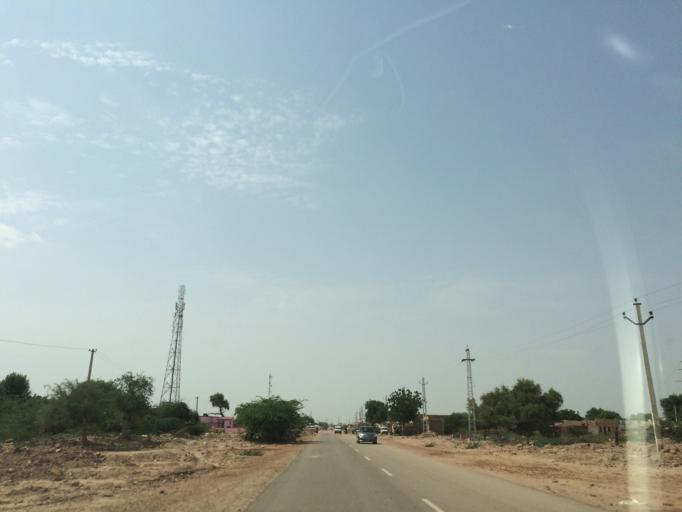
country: IN
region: Rajasthan
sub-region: Jaisalmer
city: Jaisalmer
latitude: 26.6976
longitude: 71.1981
